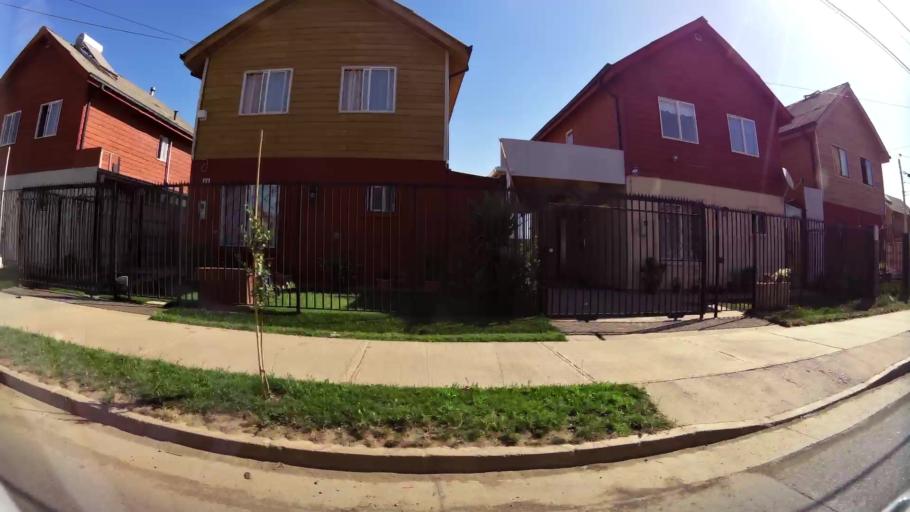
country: CL
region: Maule
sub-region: Provincia de Talca
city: Talca
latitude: -35.4164
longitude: -71.6113
